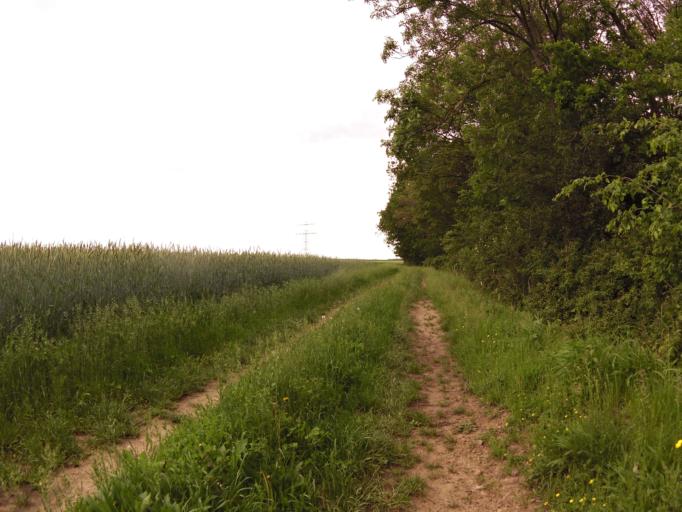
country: DE
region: Bavaria
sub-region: Regierungsbezirk Unterfranken
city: Theilheim
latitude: 49.7265
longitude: 10.0541
